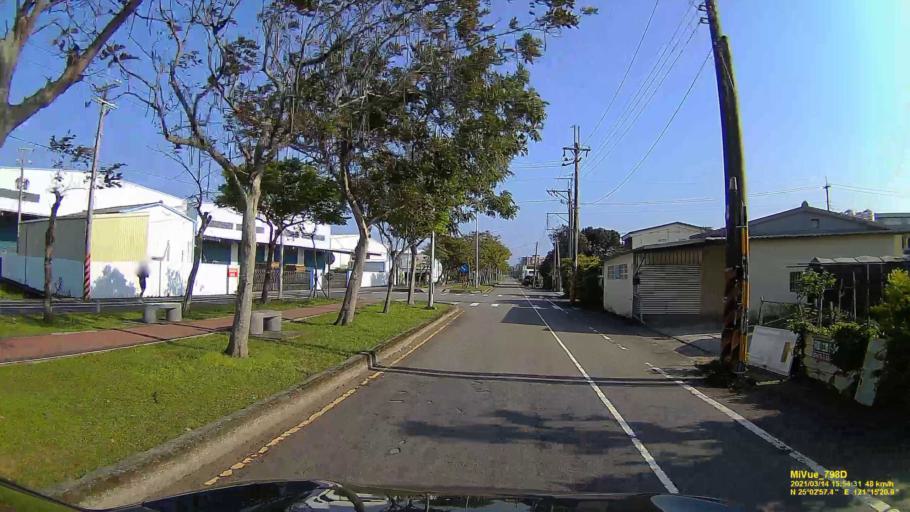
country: TW
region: Taiwan
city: Taoyuan City
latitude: 25.0491
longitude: 121.2559
